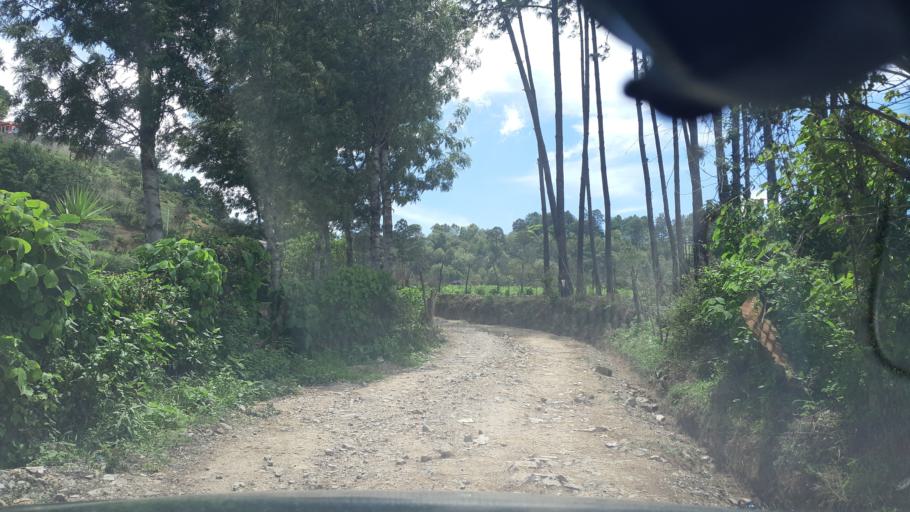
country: GT
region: Chimaltenango
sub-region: Municipio de Chimaltenango
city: Chimaltenango
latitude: 14.6608
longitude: -90.8486
